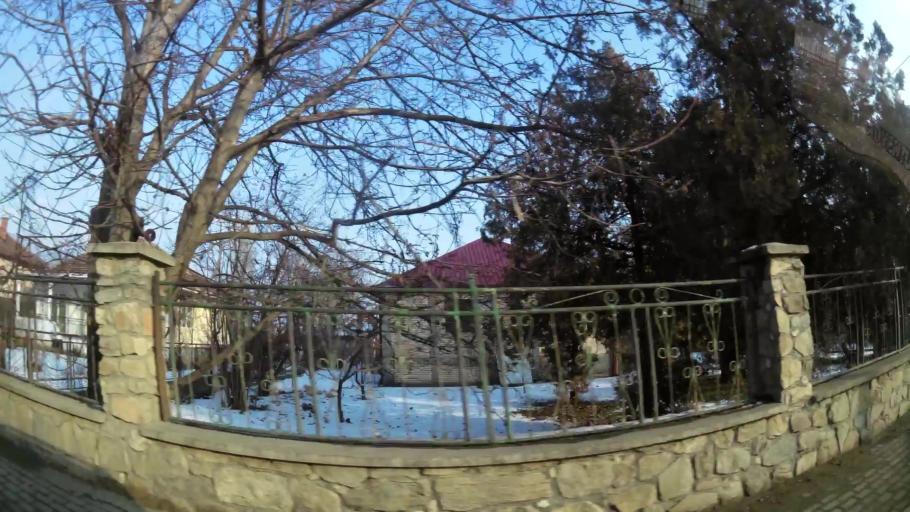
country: MK
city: Creshevo
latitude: 42.0240
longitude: 21.5149
